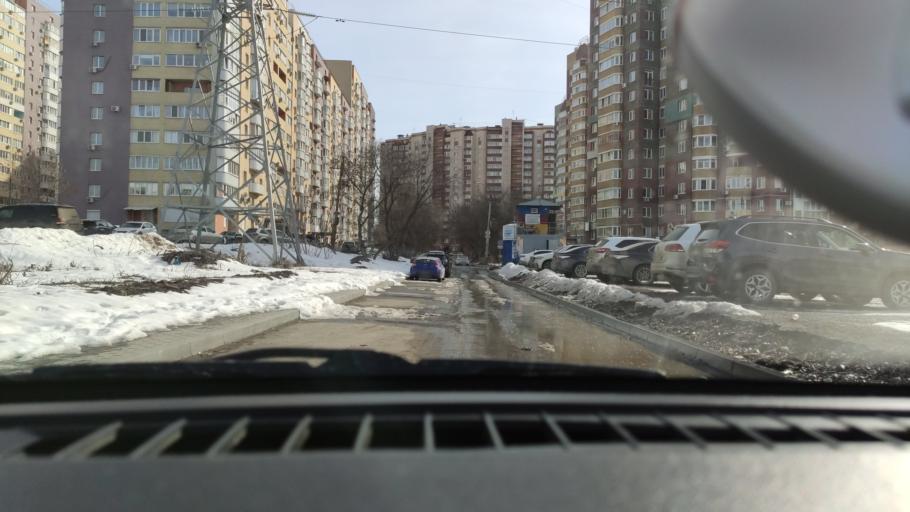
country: RU
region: Samara
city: Samara
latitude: 53.2488
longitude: 50.1909
